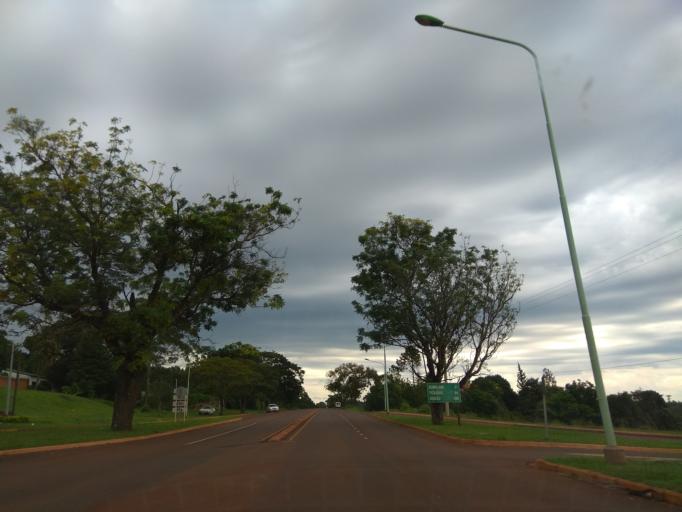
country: AR
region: Misiones
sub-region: Departamento de Leandro N. Alem
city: Leandro N. Alem
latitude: -27.6040
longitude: -55.3396
